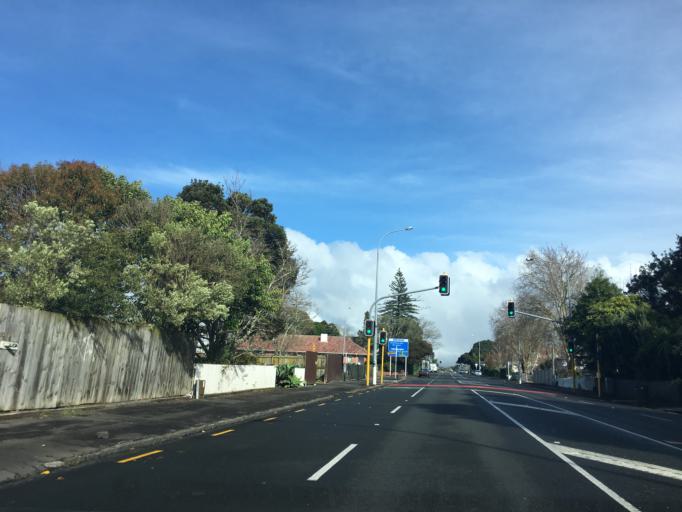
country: NZ
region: Auckland
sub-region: Auckland
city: Auckland
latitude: -36.8767
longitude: 174.7308
